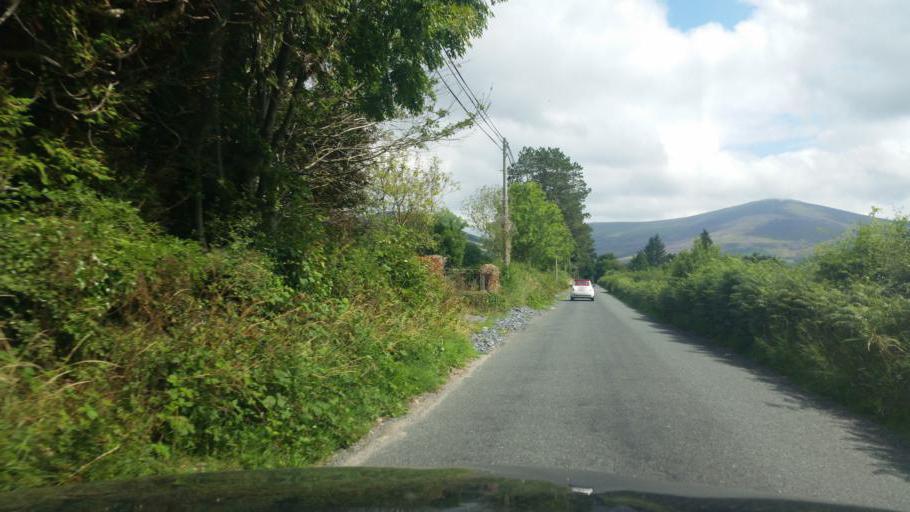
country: IE
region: Leinster
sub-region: Kilkenny
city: Graiguenamanagh
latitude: 52.6100
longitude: -6.8726
